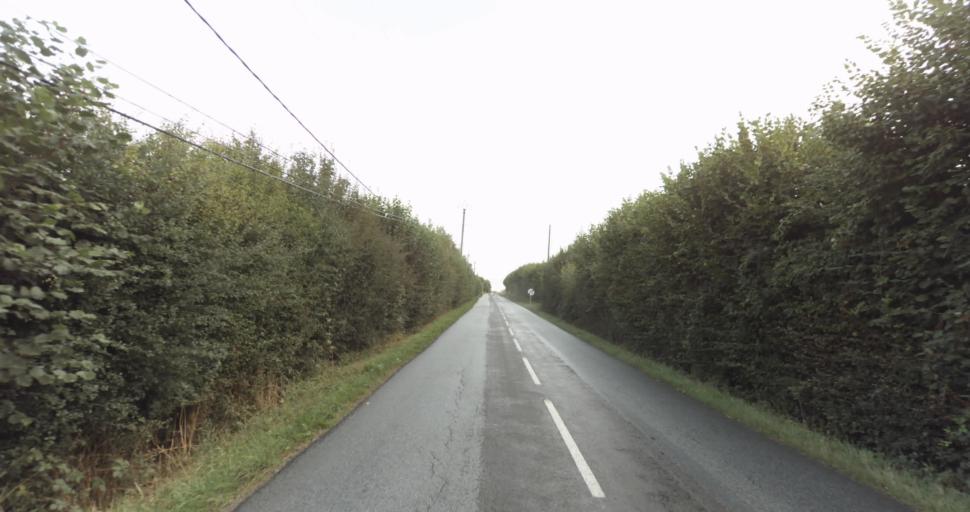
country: FR
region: Lower Normandy
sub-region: Departement de l'Orne
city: Sainte-Gauburge-Sainte-Colombe
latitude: 48.7261
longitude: 0.4313
